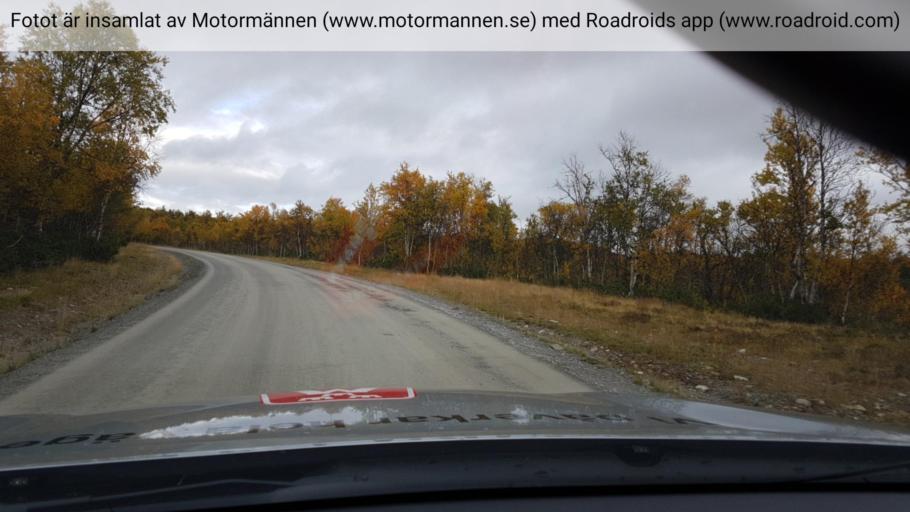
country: SE
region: Jaemtland
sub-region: Are Kommun
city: Are
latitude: 62.6152
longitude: 12.6263
